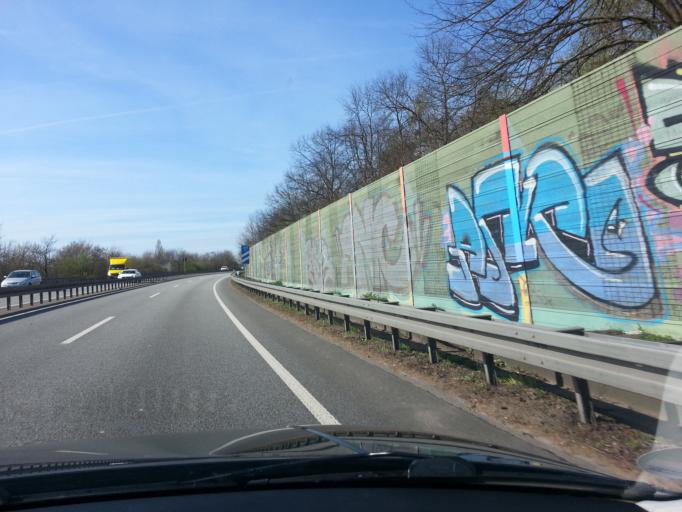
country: DE
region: Saarland
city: Sulzbach
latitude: 49.3065
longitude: 7.0604
